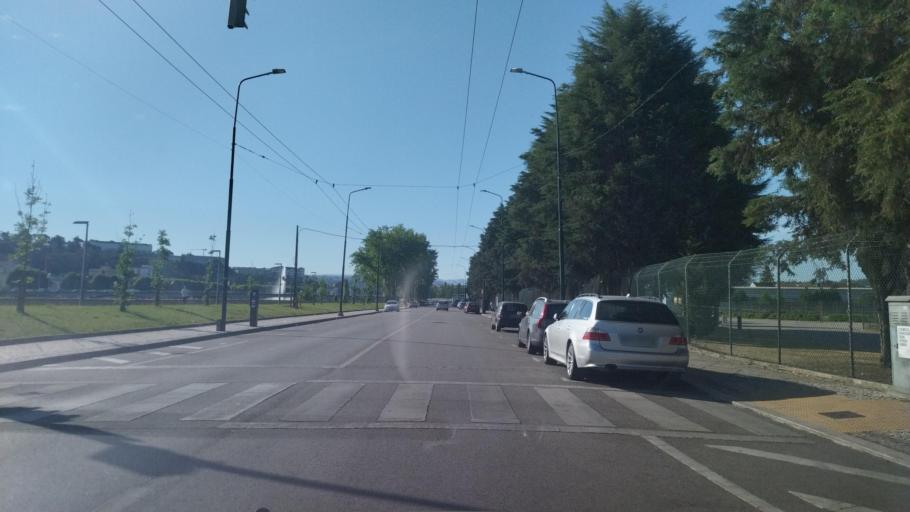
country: PT
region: Coimbra
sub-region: Coimbra
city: Coimbra
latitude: 40.2077
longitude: -8.4347
